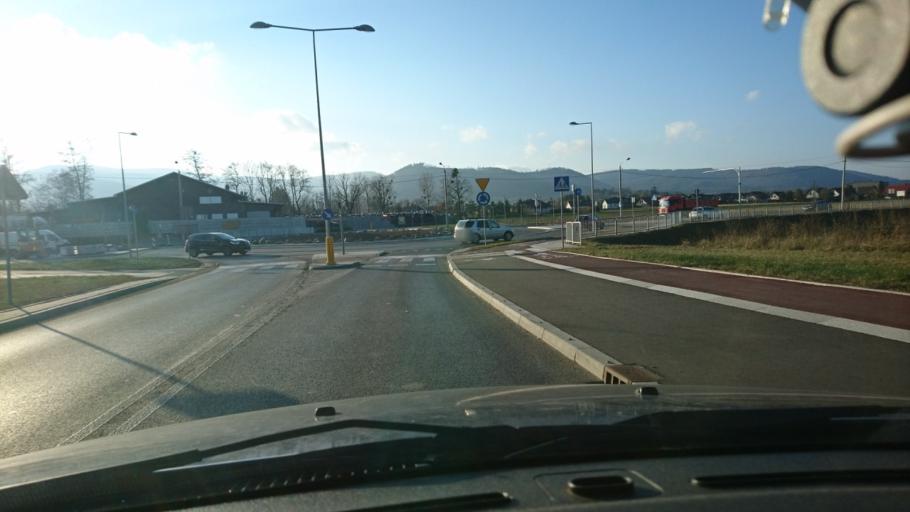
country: PL
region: Silesian Voivodeship
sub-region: Powiat bielski
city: Jaworze
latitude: 49.8081
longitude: 18.9751
